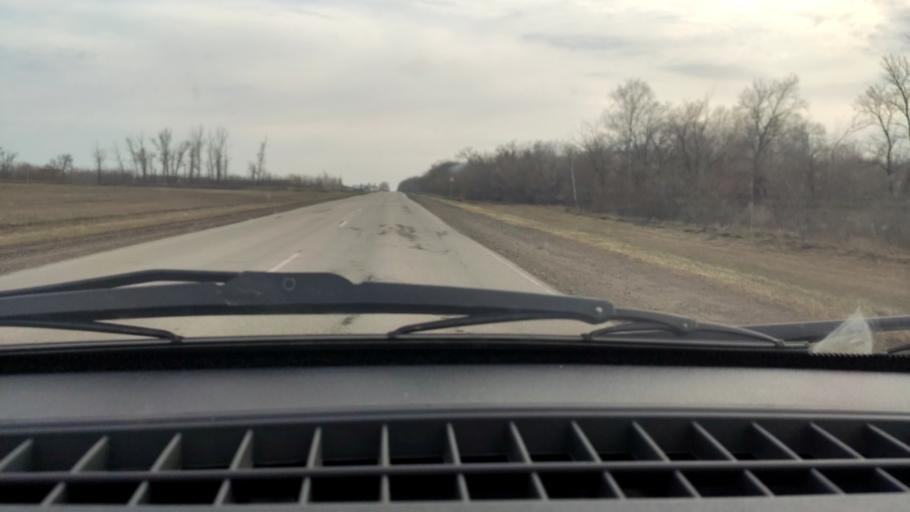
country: RU
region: Bashkortostan
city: Davlekanovo
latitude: 54.2849
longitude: 55.1136
